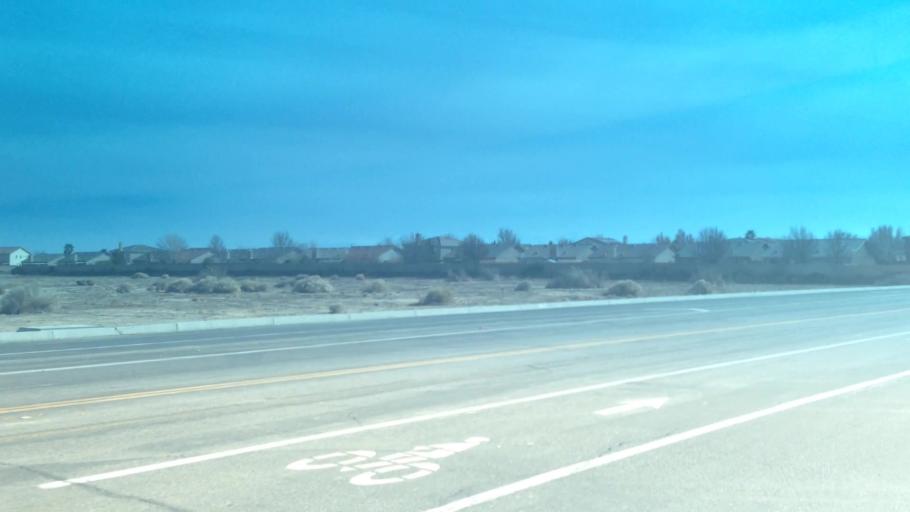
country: US
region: California
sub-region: Los Angeles County
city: Lancaster
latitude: 34.7186
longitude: -118.1663
